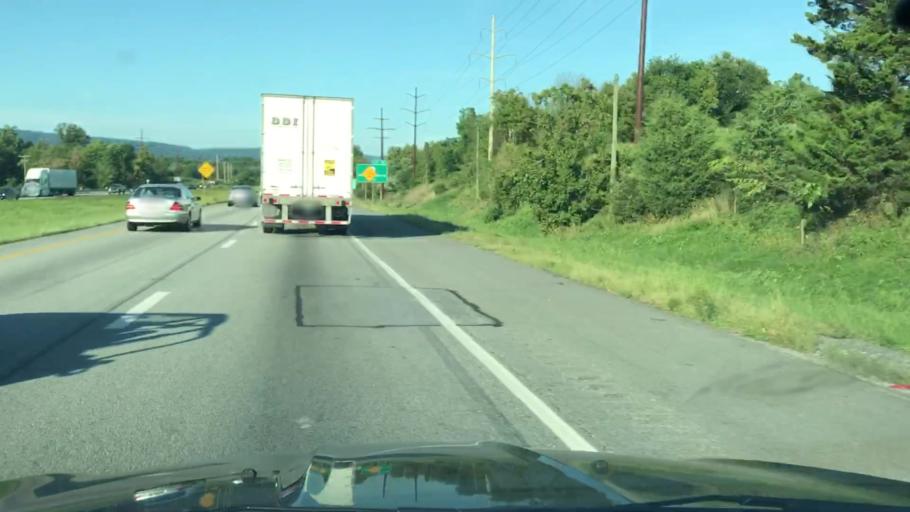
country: US
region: Pennsylvania
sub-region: Cumberland County
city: Mechanicsburg
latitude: 40.2561
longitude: -77.0690
